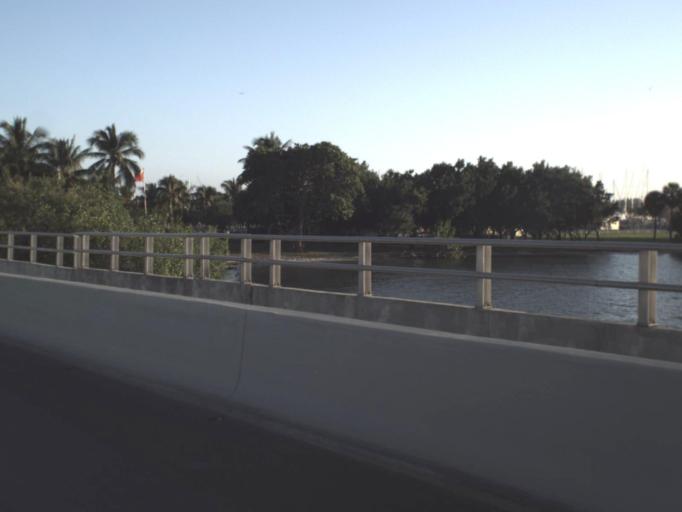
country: US
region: Florida
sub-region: Miami-Dade County
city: Key Biscayne
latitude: 25.7285
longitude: -80.1567
